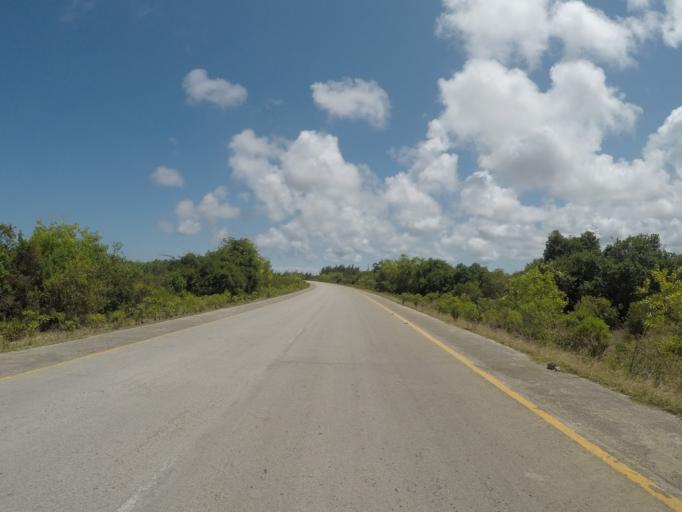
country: TZ
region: Zanzibar Central/South
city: Nganane
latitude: -6.3837
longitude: 39.5626
